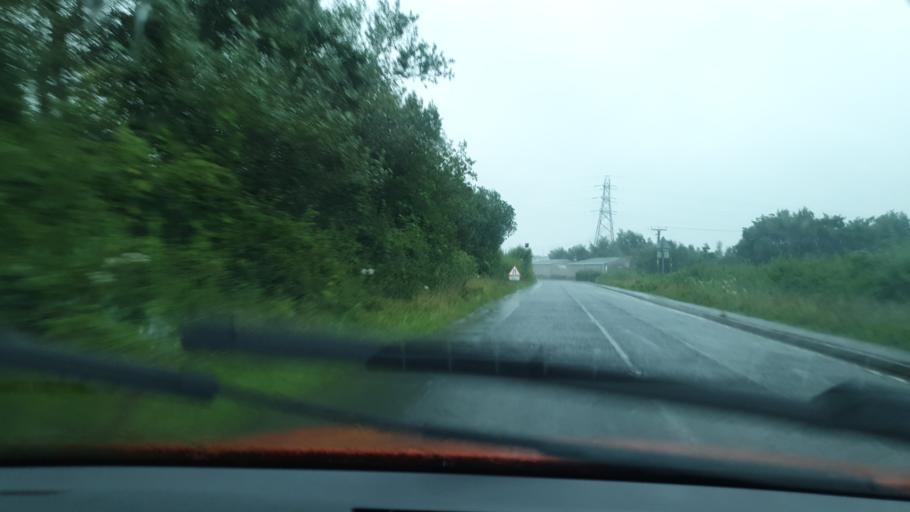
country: GB
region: England
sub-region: Cumbria
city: Millom
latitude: 54.2631
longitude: -3.2162
